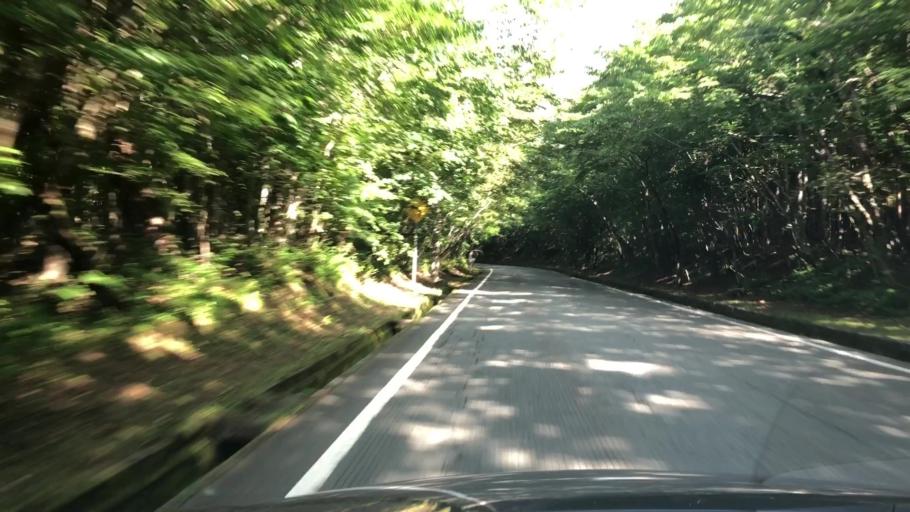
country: JP
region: Shizuoka
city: Gotemba
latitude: 35.3328
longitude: 138.8300
